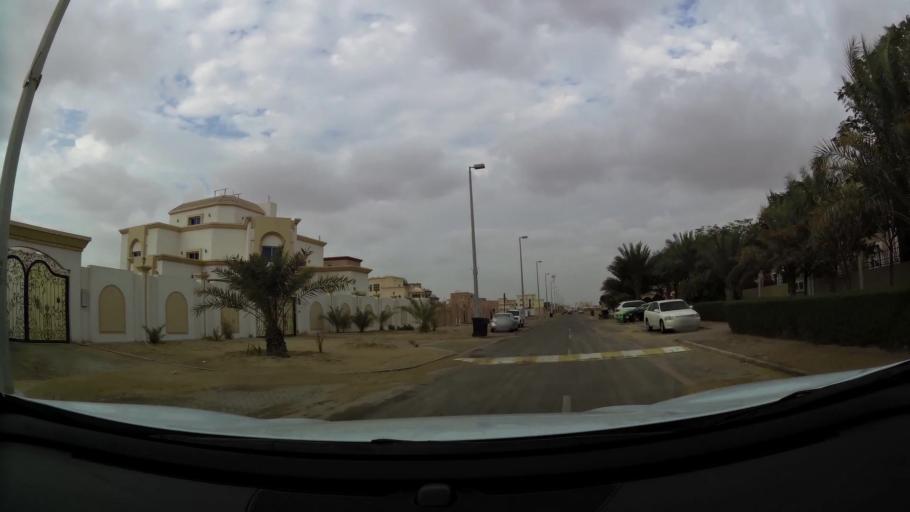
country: AE
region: Abu Dhabi
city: Abu Dhabi
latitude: 24.3452
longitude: 54.6128
